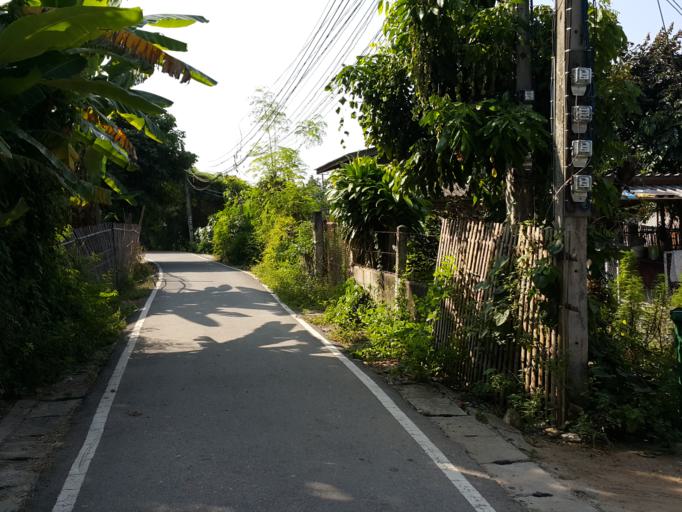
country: TH
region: Chiang Mai
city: San Kamphaeng
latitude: 18.7727
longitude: 99.0946
